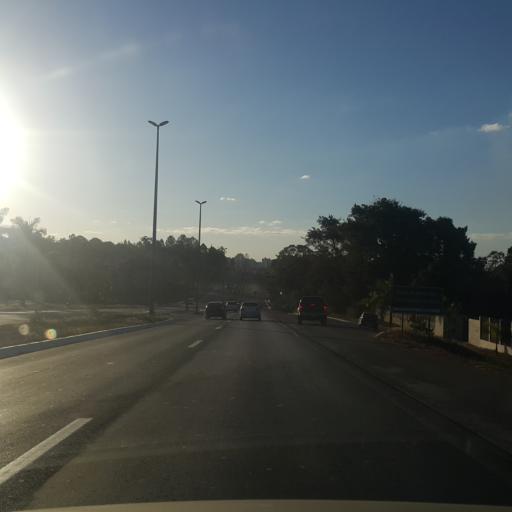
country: BR
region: Federal District
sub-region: Brasilia
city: Brasilia
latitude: -15.8624
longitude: -47.9845
